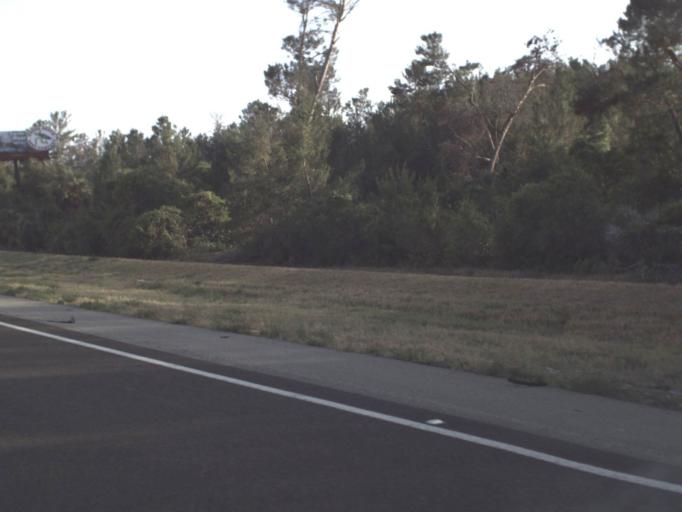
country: US
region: Florida
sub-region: Brevard County
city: Mims
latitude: 28.6211
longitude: -80.8515
